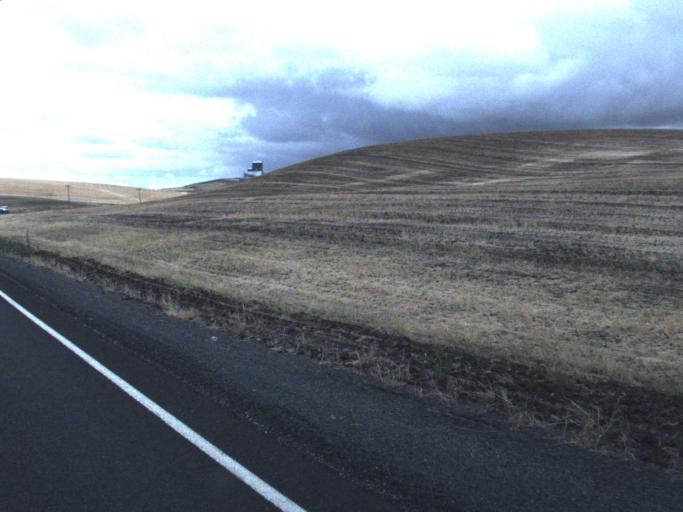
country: US
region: Washington
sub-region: Whitman County
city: Colfax
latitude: 47.1870
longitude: -117.3186
